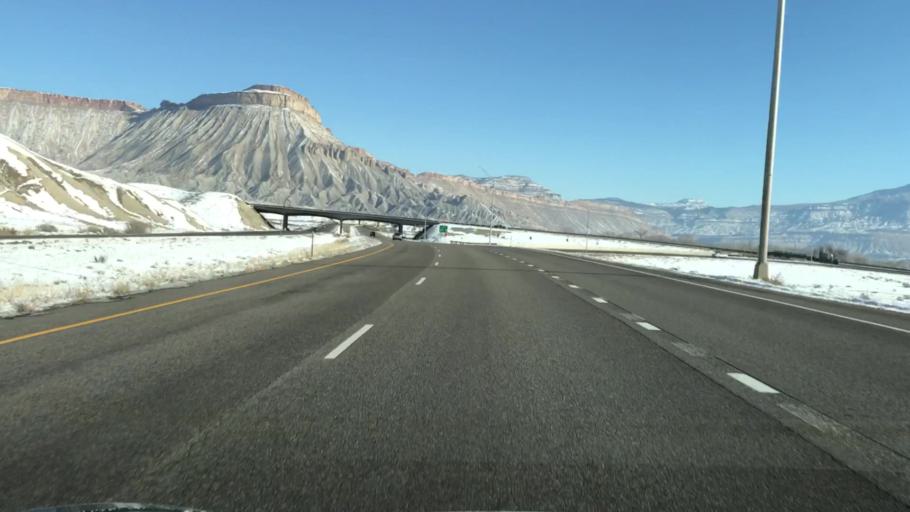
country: US
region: Colorado
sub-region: Mesa County
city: Clifton
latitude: 39.1025
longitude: -108.4503
